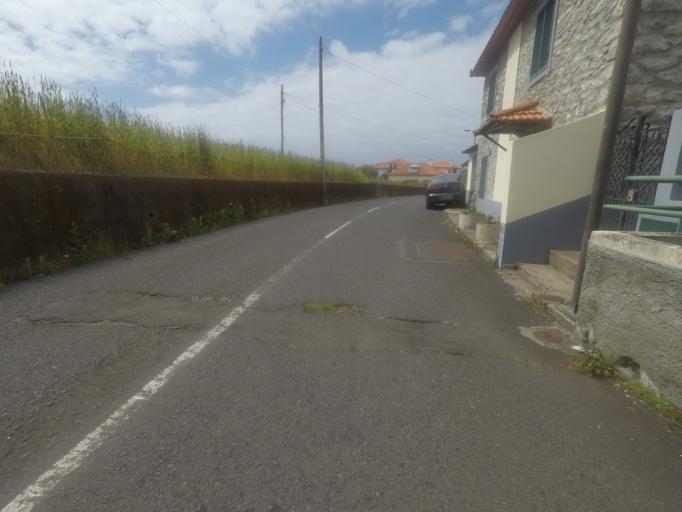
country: PT
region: Madeira
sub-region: Santana
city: Santana
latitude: 32.8108
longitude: -16.8861
